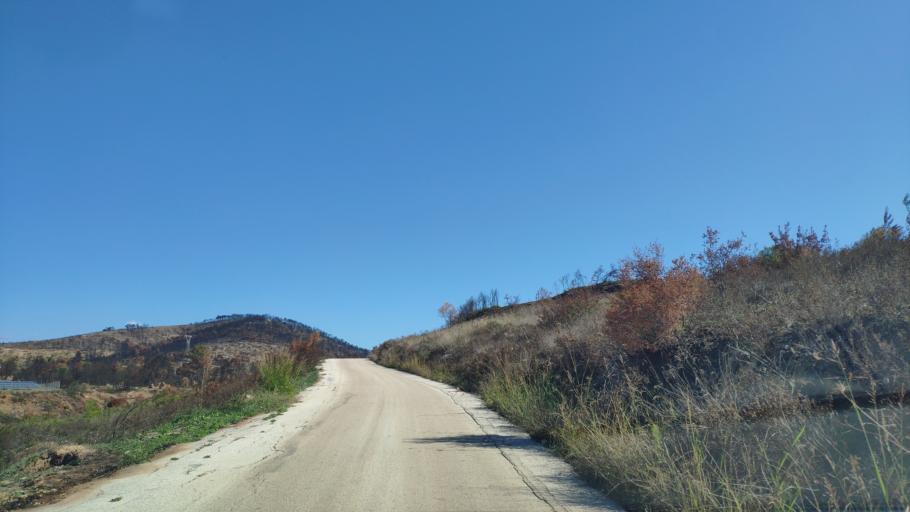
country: GR
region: Peloponnese
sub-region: Nomos Korinthias
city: Athikia
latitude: 37.8448
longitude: 22.9326
